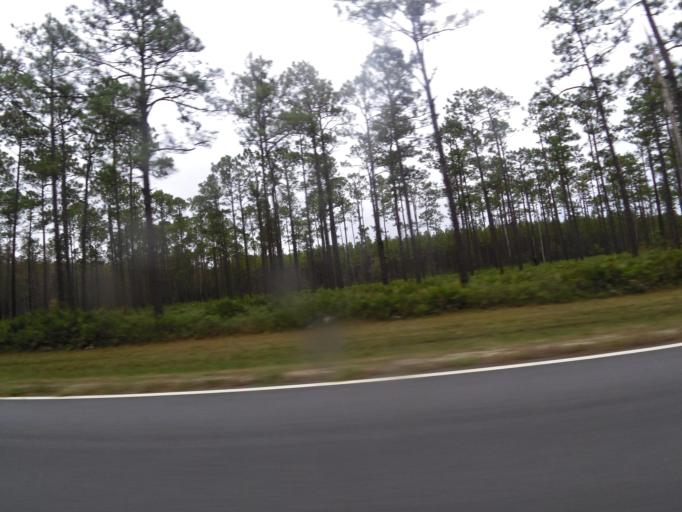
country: US
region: Georgia
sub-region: Charlton County
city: Folkston
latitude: 30.7400
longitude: -82.0905
